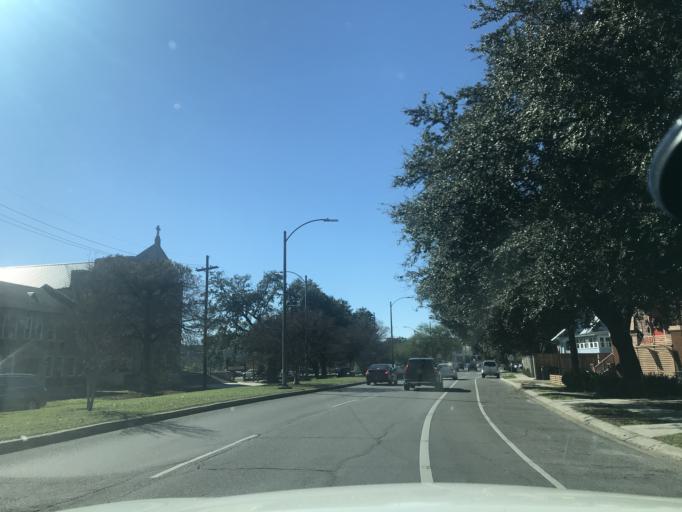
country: US
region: Louisiana
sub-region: Orleans Parish
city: New Orleans
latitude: 29.9500
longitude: -90.1026
